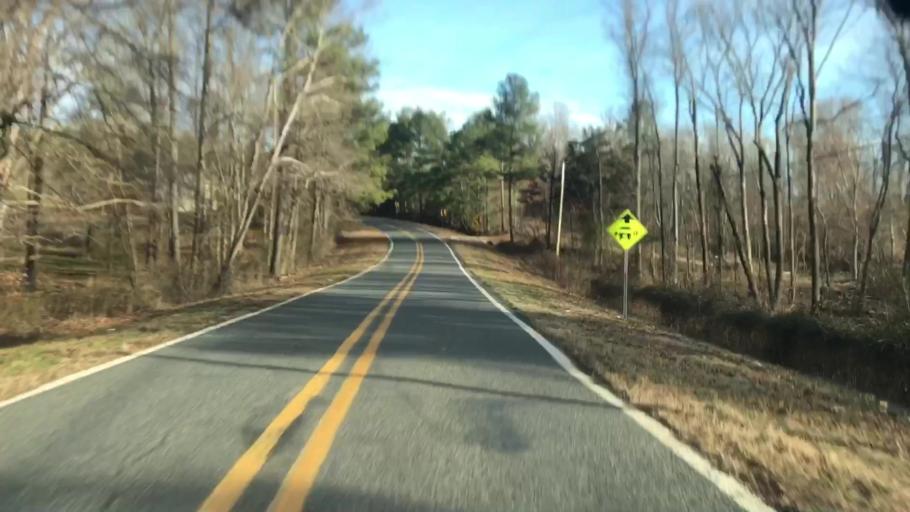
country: US
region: Arkansas
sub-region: Garland County
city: Rockwell
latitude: 34.4914
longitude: -93.2758
